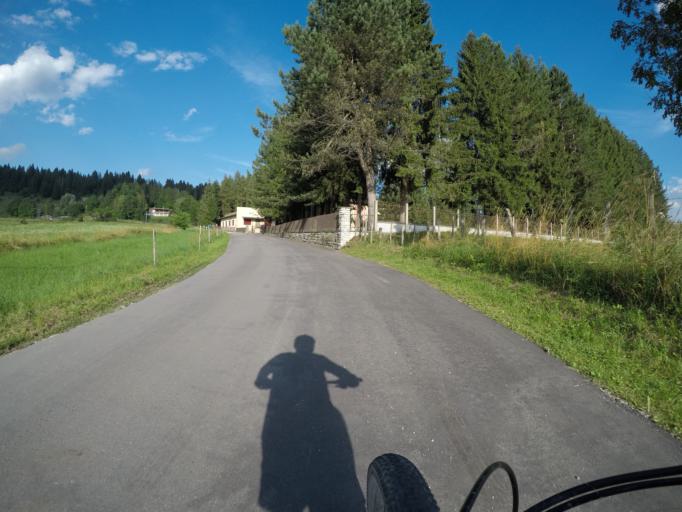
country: IT
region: Veneto
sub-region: Provincia di Vicenza
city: Gallio
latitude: 45.8867
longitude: 11.5256
